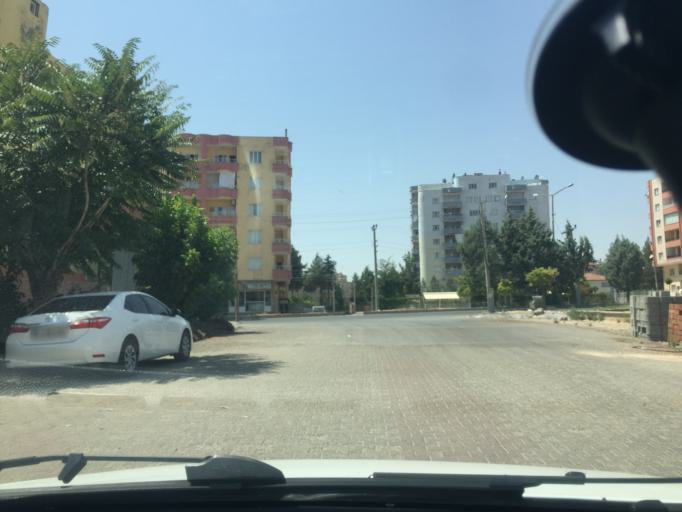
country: TR
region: Mardin
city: Midyat
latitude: 37.4266
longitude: 41.3459
